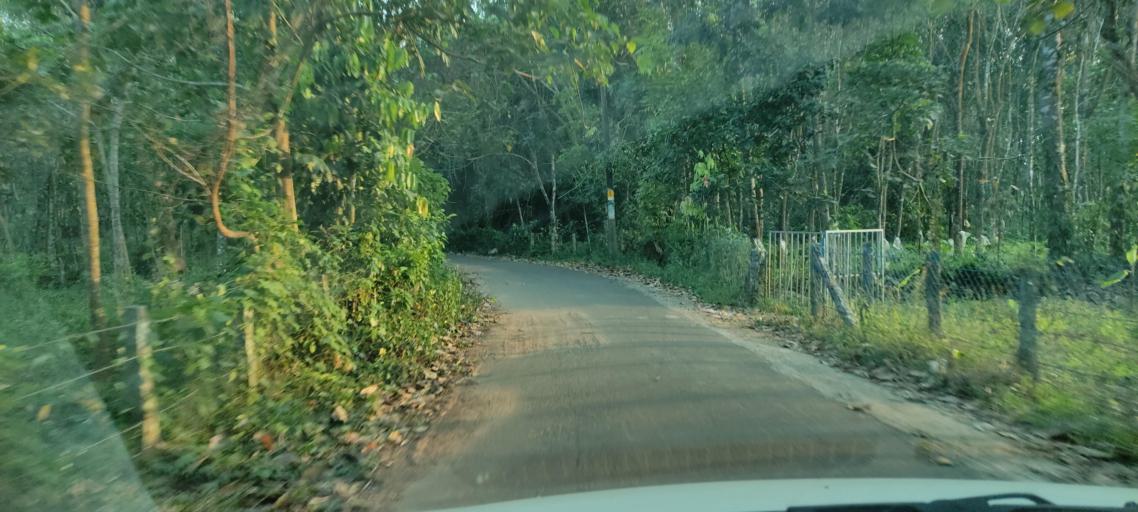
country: IN
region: Kerala
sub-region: Alappuzha
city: Kattanam
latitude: 9.1646
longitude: 76.5903
